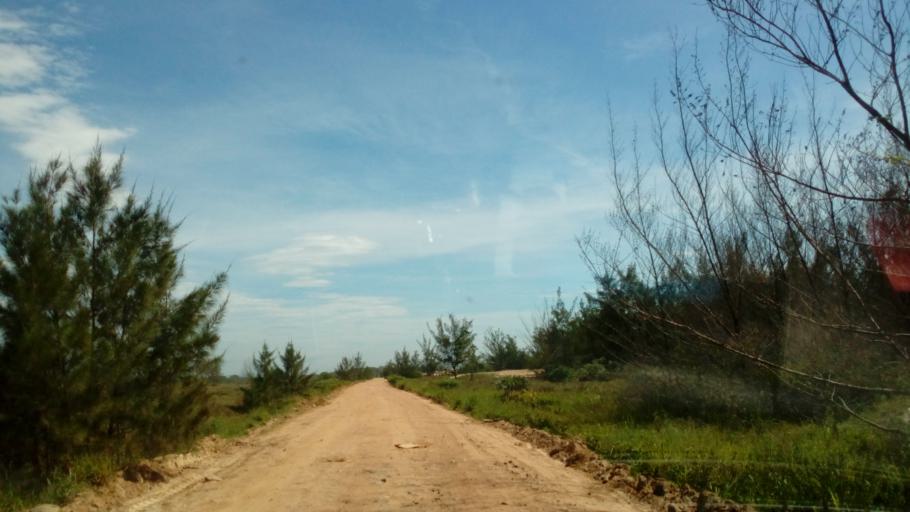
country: BR
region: Santa Catarina
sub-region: Laguna
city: Laguna
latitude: -28.4497
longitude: -48.7641
